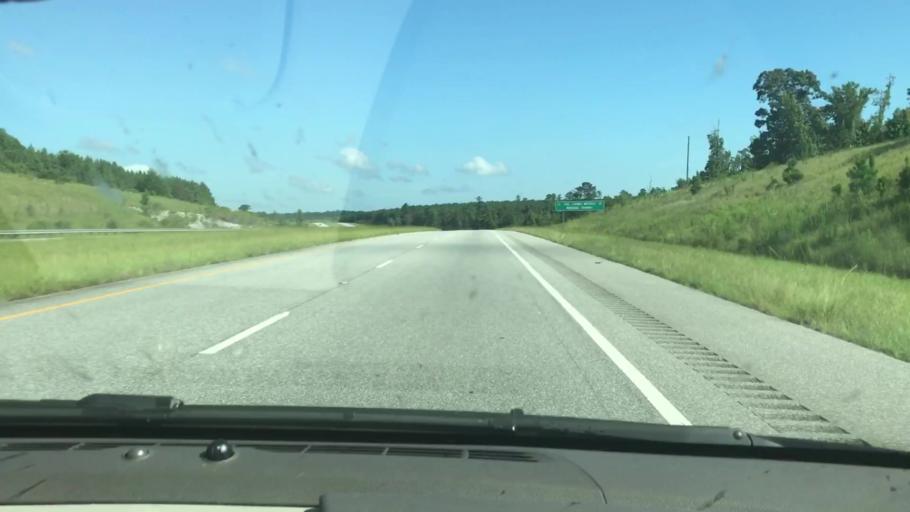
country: US
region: Alabama
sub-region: Barbour County
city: Eufaula
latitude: 32.1117
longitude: -85.1500
